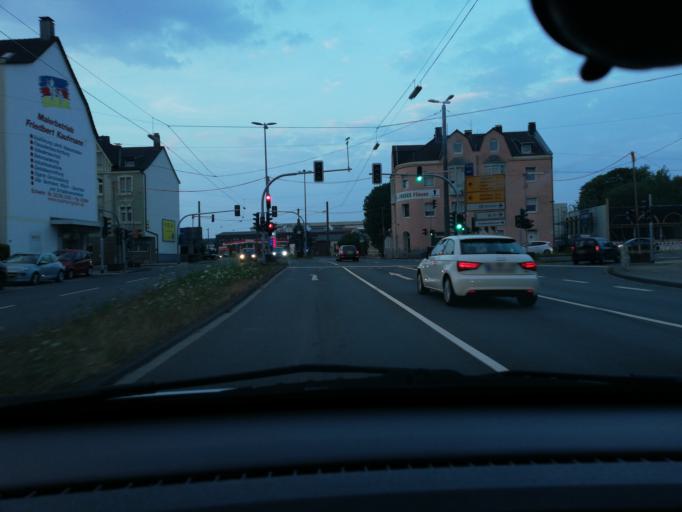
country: DE
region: North Rhine-Westphalia
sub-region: Regierungsbezirk Arnsberg
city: Schwelm
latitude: 51.2930
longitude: 7.2872
